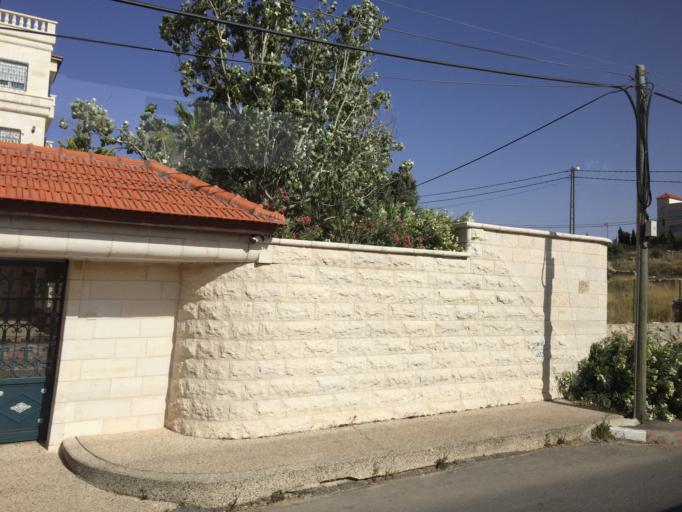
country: PS
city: Ad Dawhah
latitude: 31.7119
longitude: 35.1746
